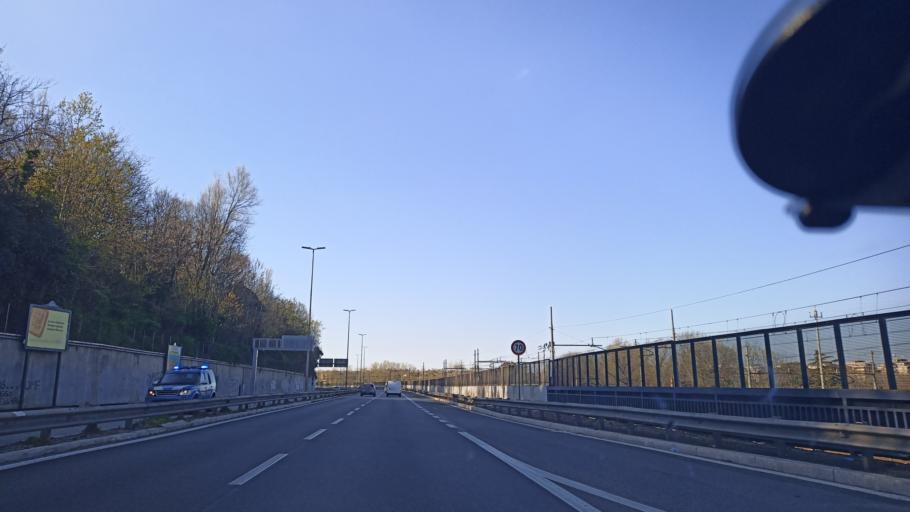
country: IT
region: Latium
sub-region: Citta metropolitana di Roma Capitale
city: Rome
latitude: 41.9353
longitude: 12.5205
